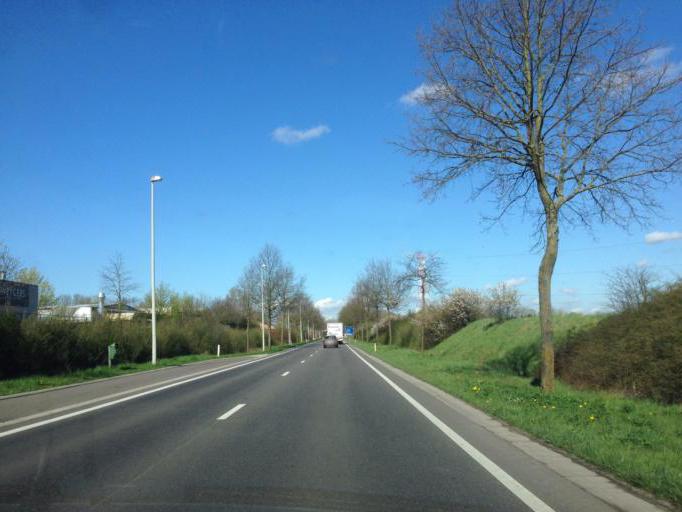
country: BE
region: Flanders
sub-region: Provincie Limburg
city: Peer
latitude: 51.1354
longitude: 5.4716
